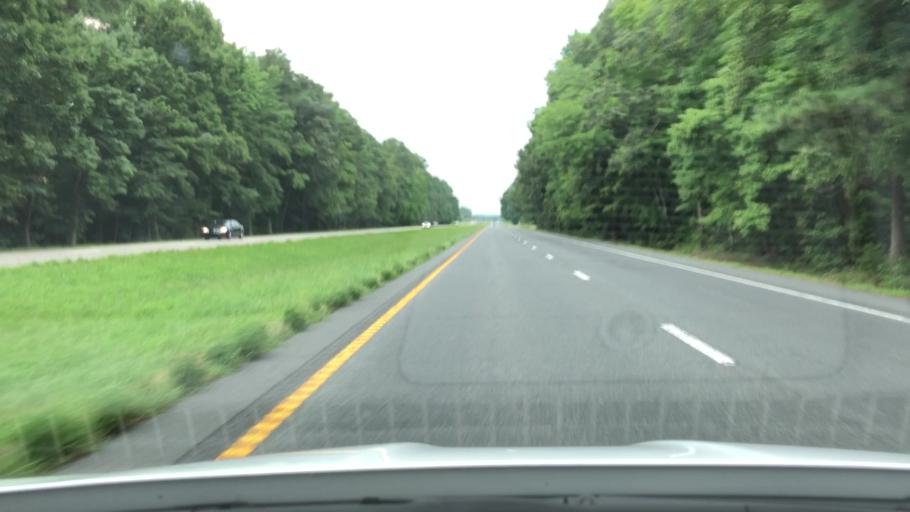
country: US
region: Virginia
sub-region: Northampton County
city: Eastville
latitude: 37.3455
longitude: -75.9409
